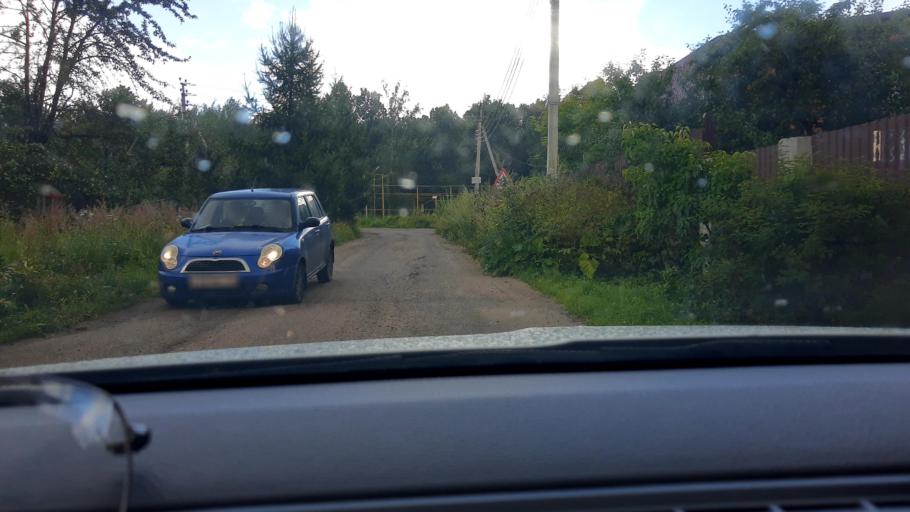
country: RU
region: Moskovskaya
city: Nemchinovka
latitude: 55.7334
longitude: 37.3550
